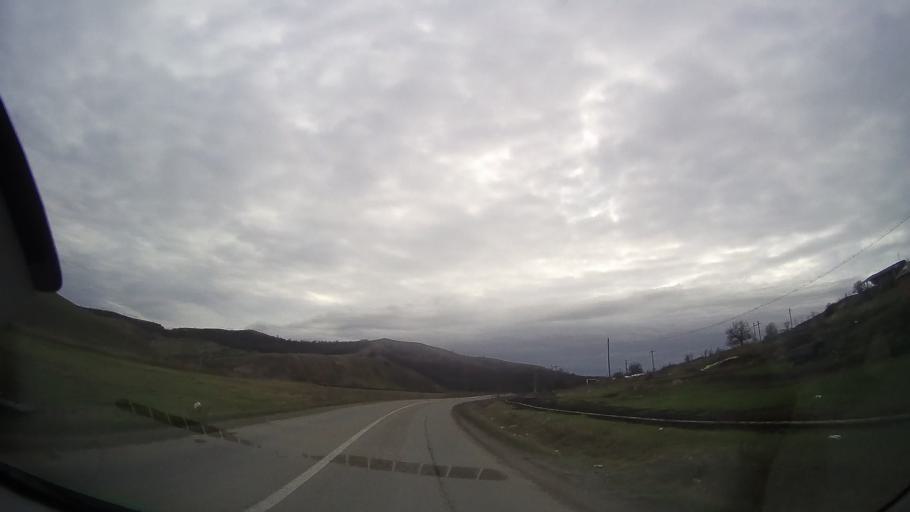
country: RO
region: Bistrita-Nasaud
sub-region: Comuna Budesti
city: Budesti
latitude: 46.8683
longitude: 24.2460
